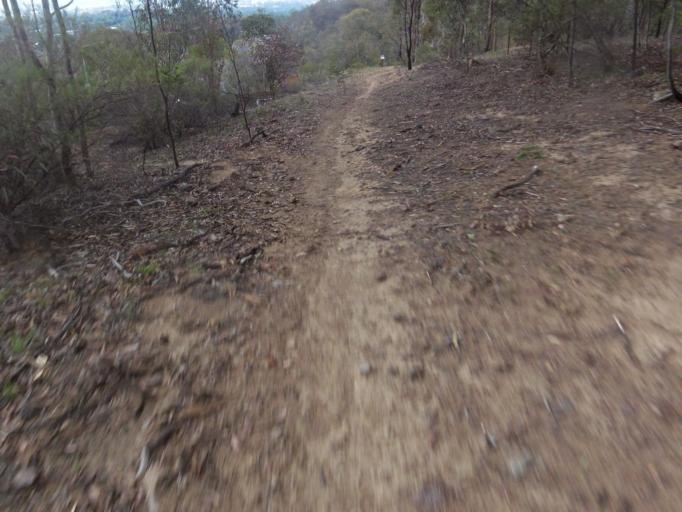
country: AU
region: Australian Capital Territory
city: Forrest
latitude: -35.3476
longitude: 149.1270
